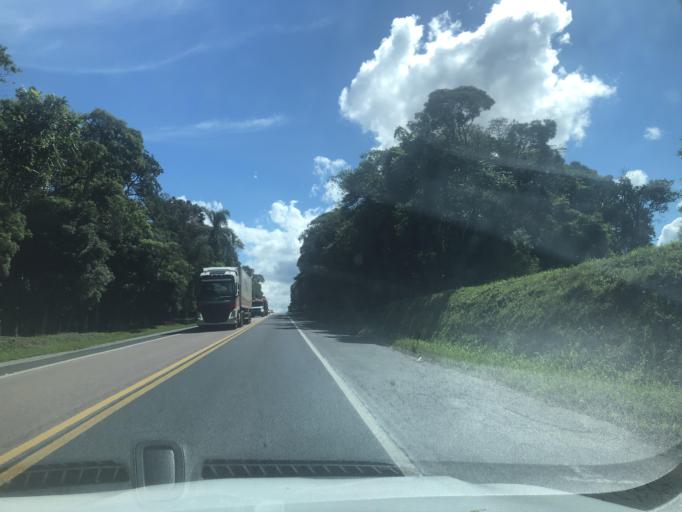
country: BR
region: Santa Catarina
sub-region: Canoinhas
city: Canoinhas
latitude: -26.3833
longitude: -50.2172
